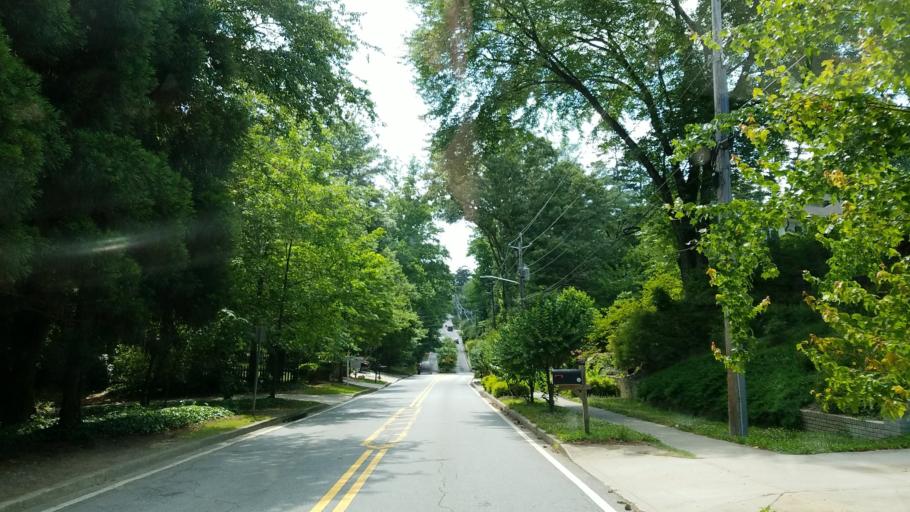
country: US
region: Georgia
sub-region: DeKalb County
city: North Atlanta
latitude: 33.8286
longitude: -84.3757
